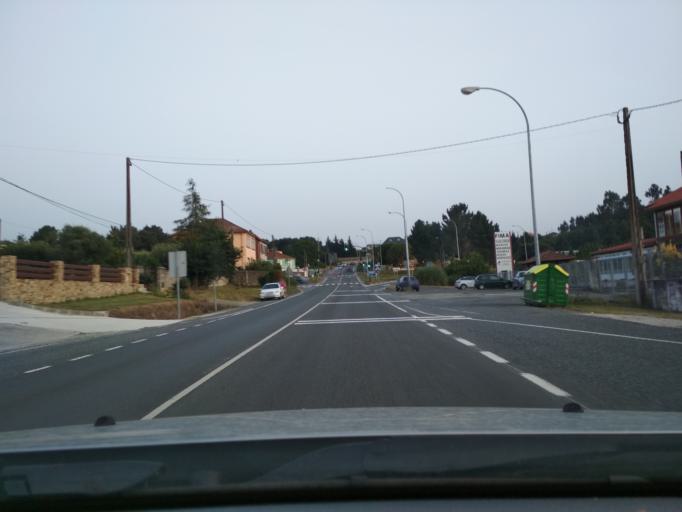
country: ES
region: Galicia
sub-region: Provincia da Coruna
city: Cambre
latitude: 43.2772
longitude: -8.3651
